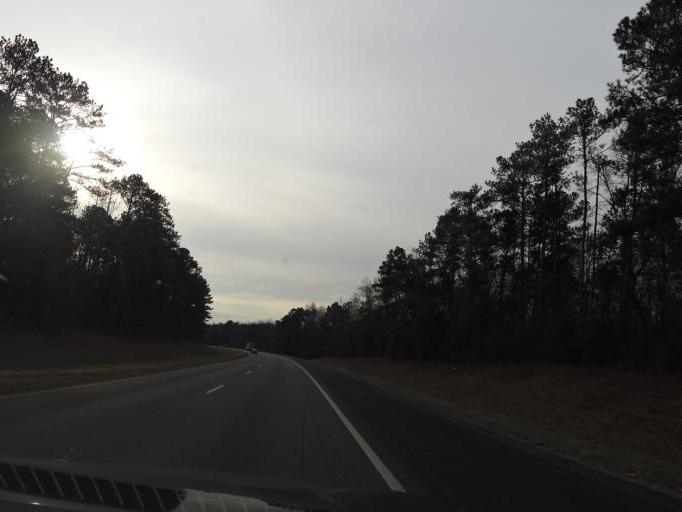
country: US
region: Alabama
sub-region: Autauga County
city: Pine Level
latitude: 32.5250
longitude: -86.4418
